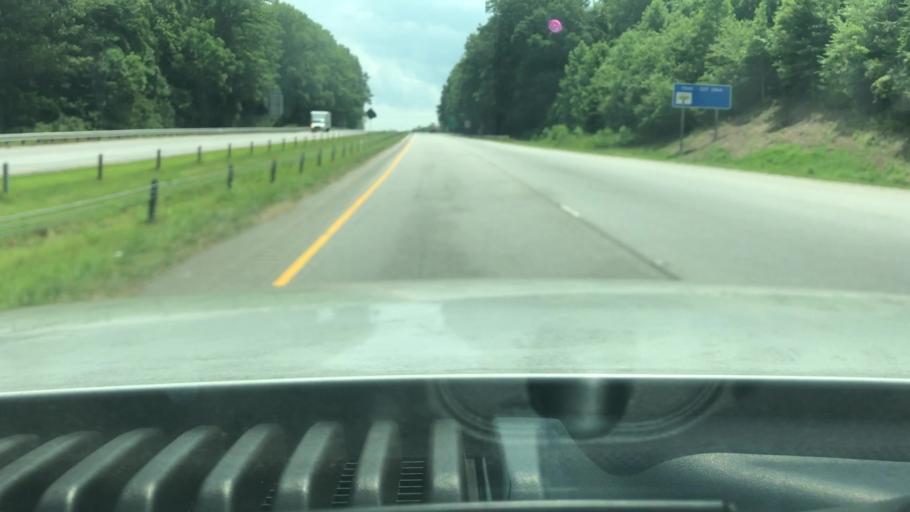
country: US
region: North Carolina
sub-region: Wilkes County
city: Wilkesboro
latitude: 36.1385
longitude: -81.1698
